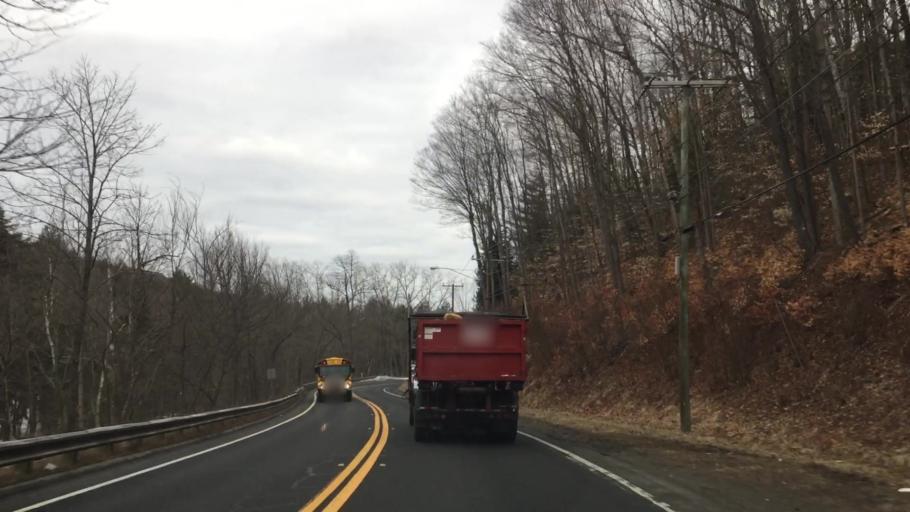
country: US
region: Massachusetts
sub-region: Berkshire County
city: Hinsdale
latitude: 42.4627
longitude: -73.1352
